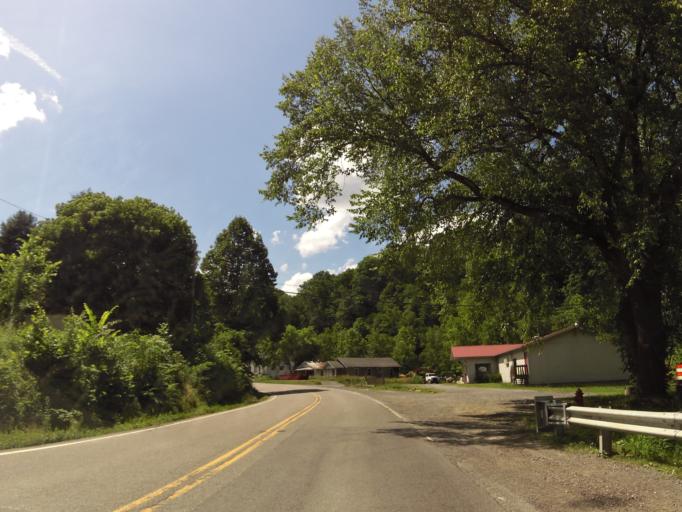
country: US
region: Virginia
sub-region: Lee County
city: Pennington Gap
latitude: 36.7774
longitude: -83.0534
